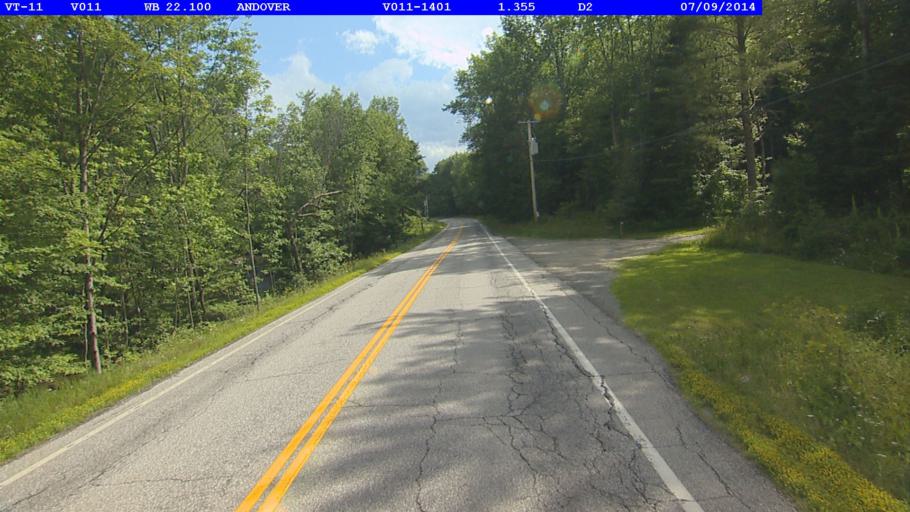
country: US
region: Vermont
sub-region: Windsor County
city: Chester
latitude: 43.2513
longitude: -72.7201
